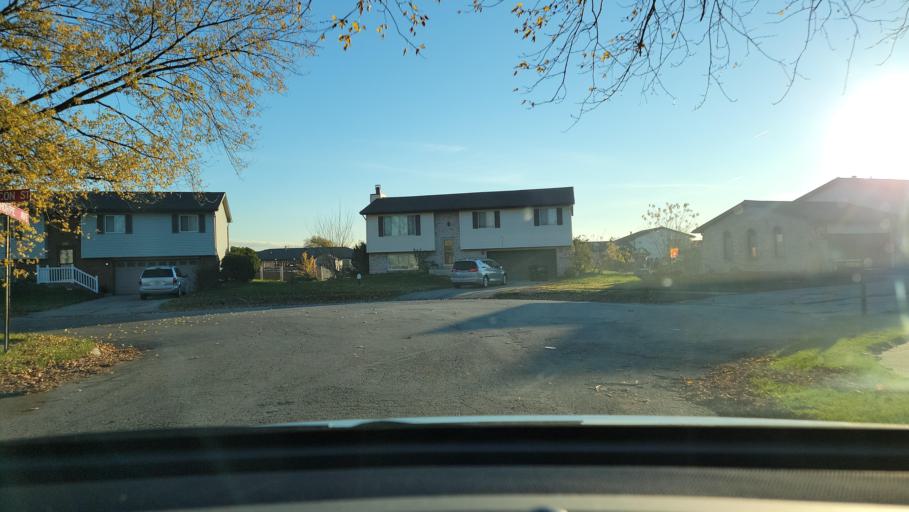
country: US
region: Indiana
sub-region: Porter County
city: Portage
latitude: 41.5594
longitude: -87.1691
